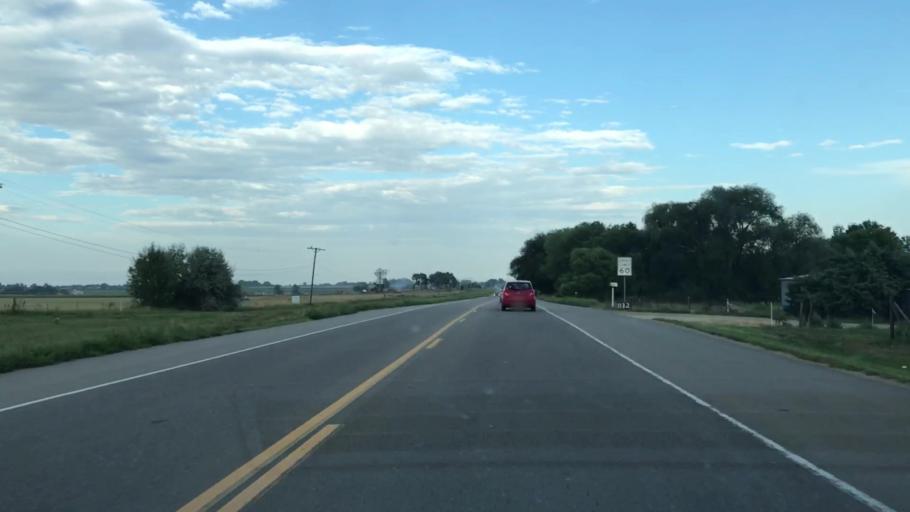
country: US
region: Colorado
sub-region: Weld County
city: Mead
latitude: 40.2039
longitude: -105.0344
